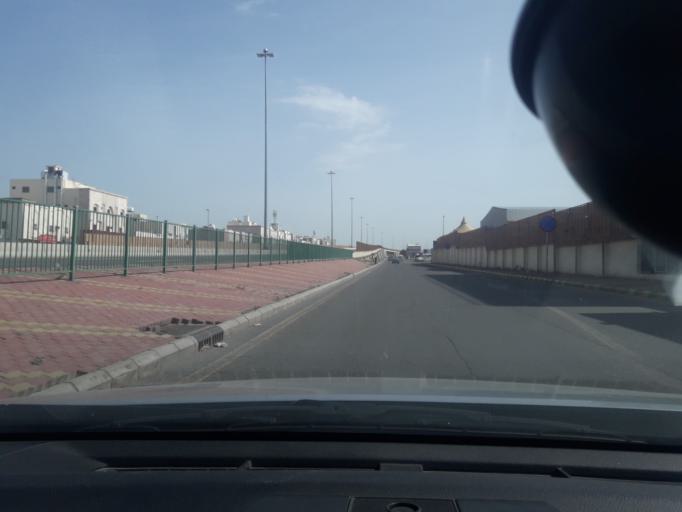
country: SA
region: Al Madinah al Munawwarah
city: Medina
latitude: 24.4490
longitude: 39.6612
